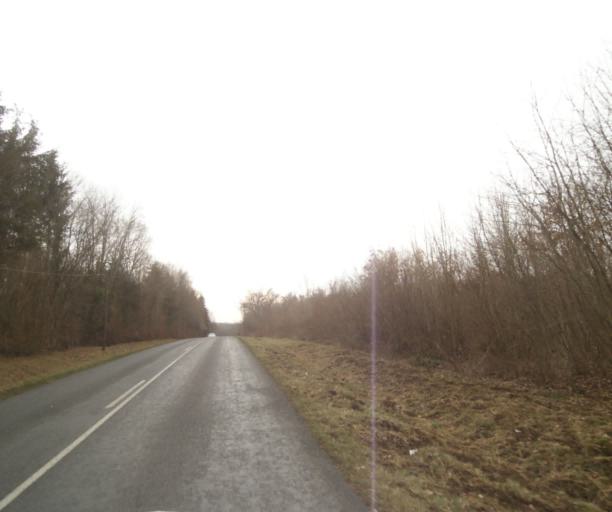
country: FR
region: Champagne-Ardenne
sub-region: Departement de la Haute-Marne
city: Villiers-en-Lieu
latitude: 48.7015
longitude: 4.8947
